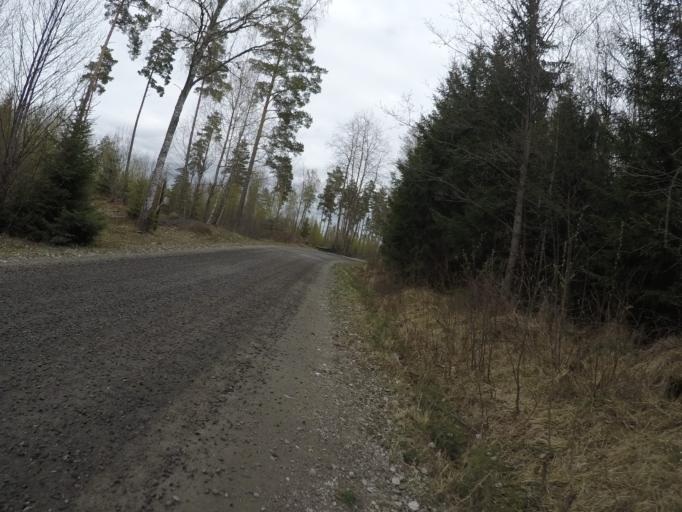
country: SE
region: Soedermanland
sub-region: Eskilstuna Kommun
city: Kvicksund
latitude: 59.3838
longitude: 16.3233
